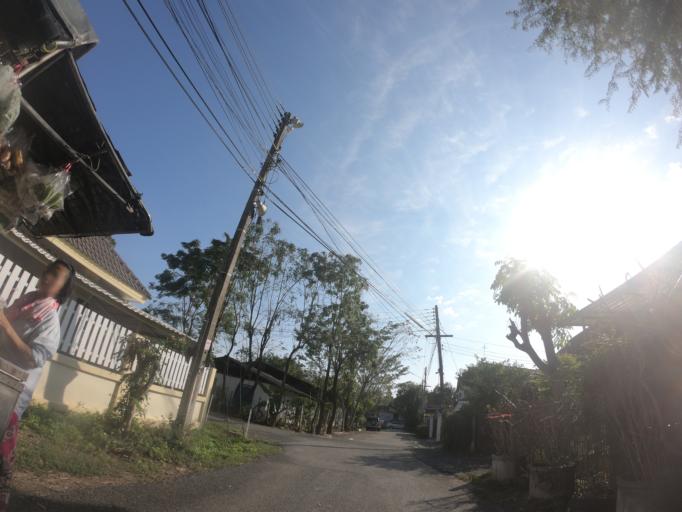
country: TH
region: Chiang Mai
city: Chiang Mai
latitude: 18.7776
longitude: 99.0336
